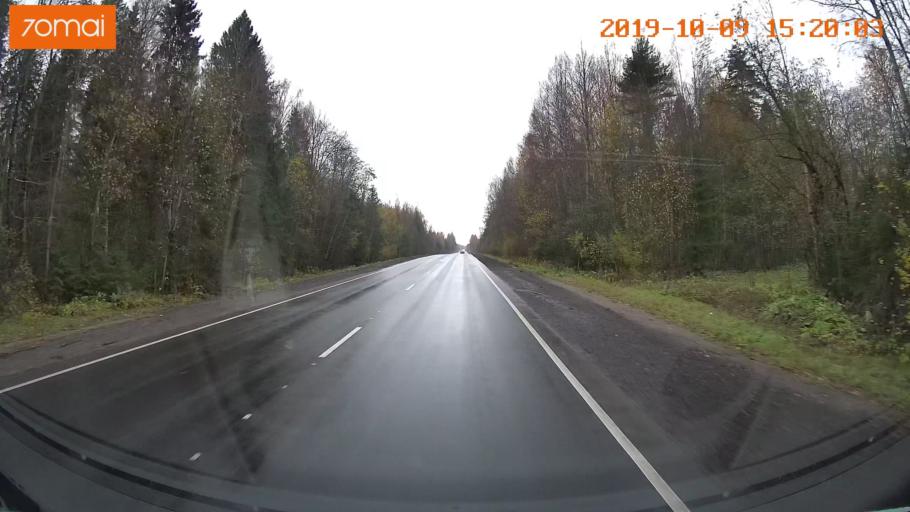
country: RU
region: Kostroma
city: Susanino
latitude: 58.0687
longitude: 41.5449
